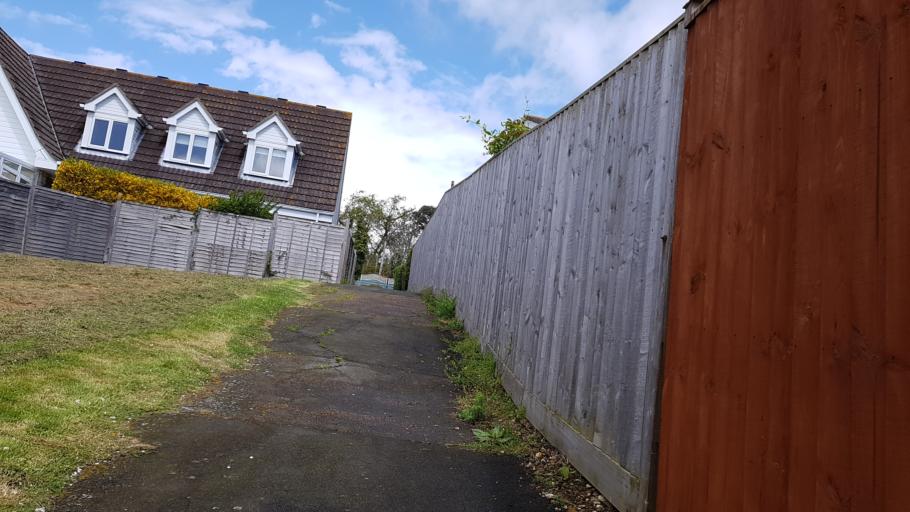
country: GB
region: England
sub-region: Isle of Wight
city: East Cowes
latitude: 50.7594
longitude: -1.2837
